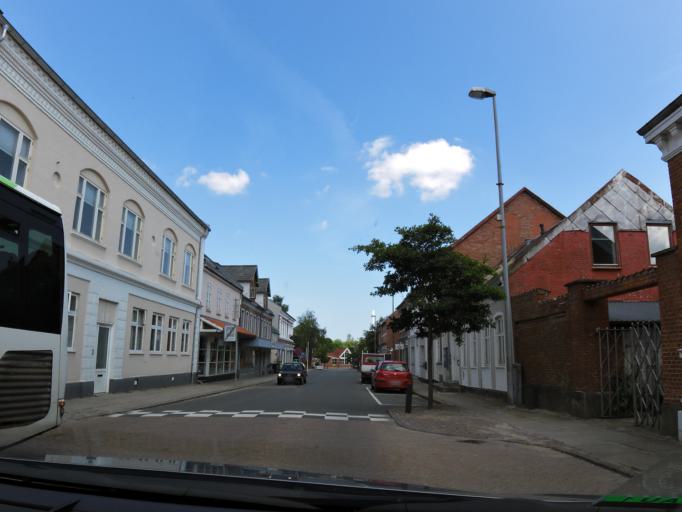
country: DK
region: South Denmark
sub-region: Assens Kommune
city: Arup
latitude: 55.3813
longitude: 10.0495
